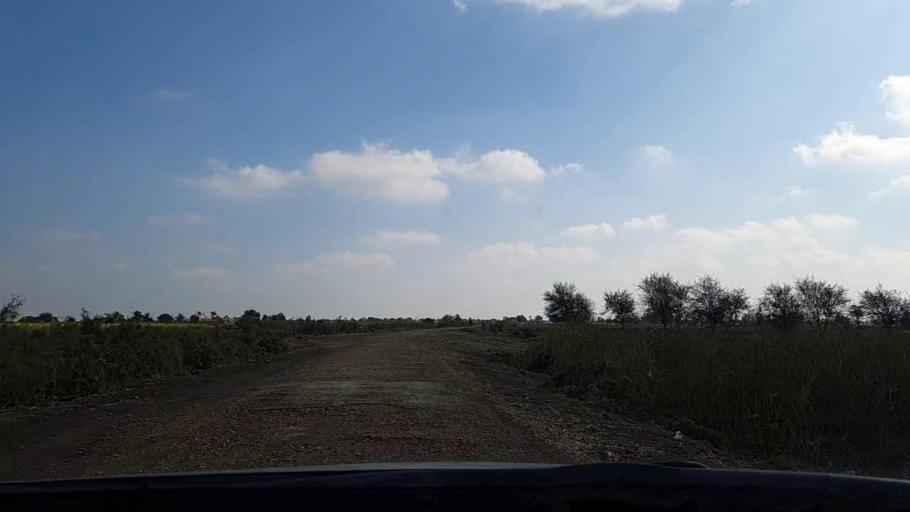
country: PK
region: Sindh
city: Pithoro
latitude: 25.7301
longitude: 69.2864
